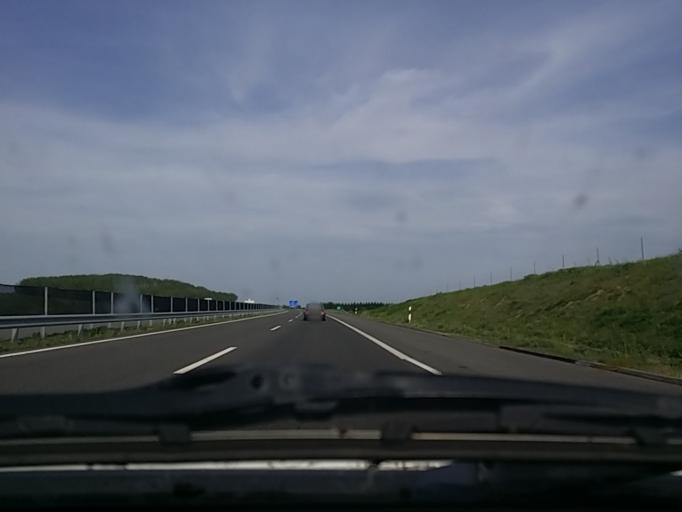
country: HU
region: Baranya
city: Kozarmisleny
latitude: 46.0125
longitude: 18.2382
